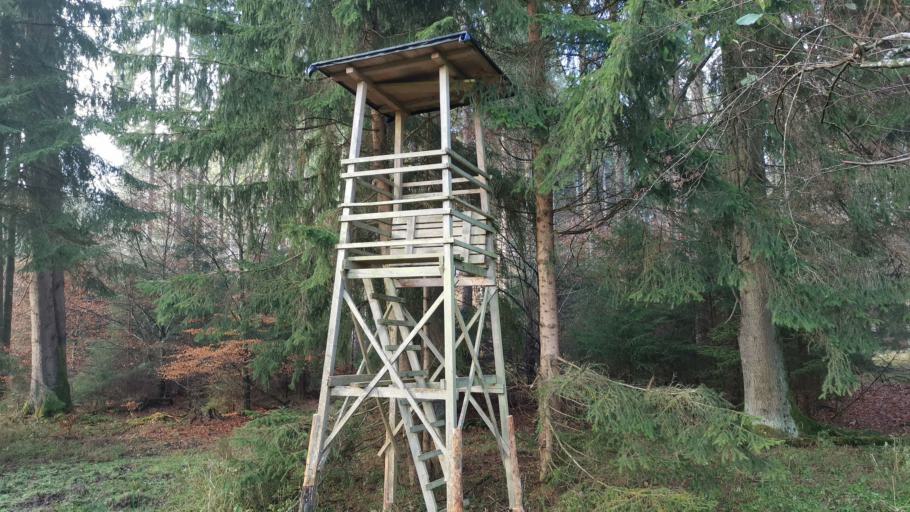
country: DE
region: Bavaria
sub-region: Upper Bavaria
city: Baierbrunn
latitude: 48.0375
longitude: 11.4775
